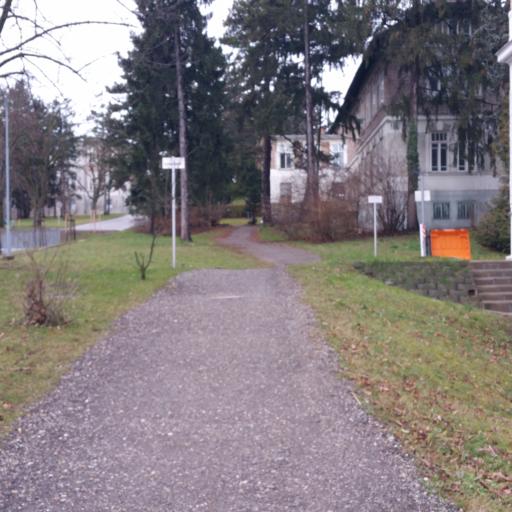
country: AT
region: Vienna
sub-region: Wien Stadt
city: Vienna
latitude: 48.2116
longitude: 16.2846
